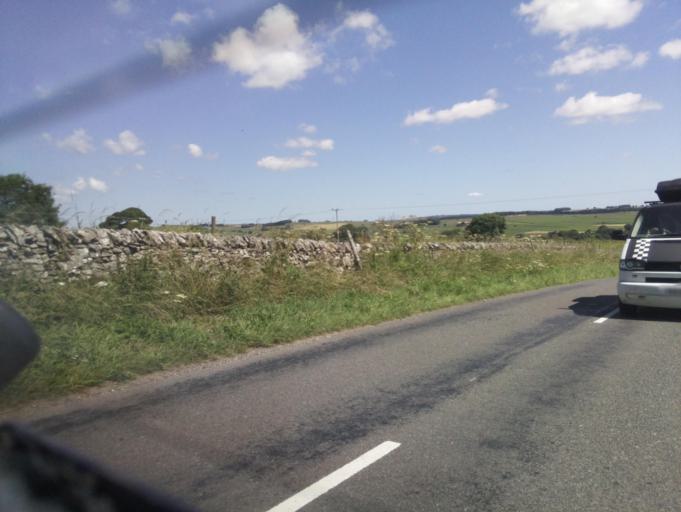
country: GB
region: England
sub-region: Derbyshire
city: Tideswell
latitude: 53.1936
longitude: -1.7903
